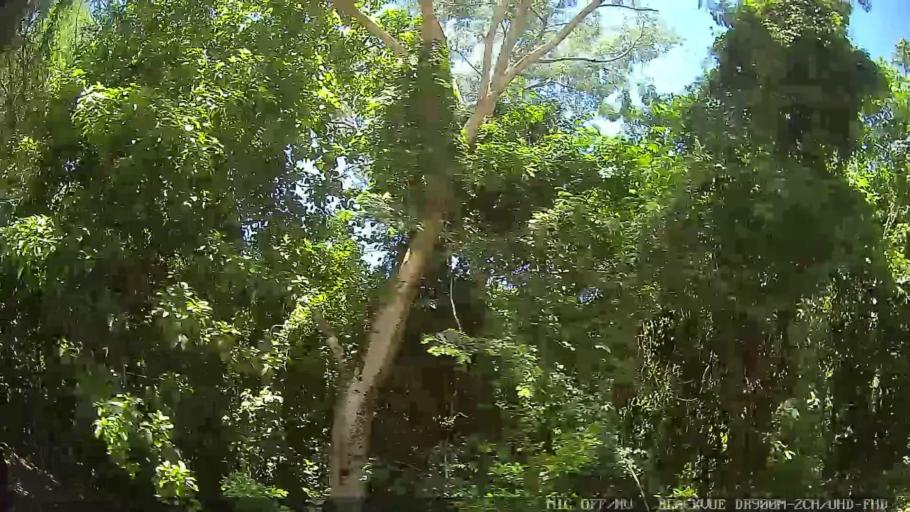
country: BR
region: Sao Paulo
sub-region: Pedreira
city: Pedreira
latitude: -22.7549
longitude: -46.9147
